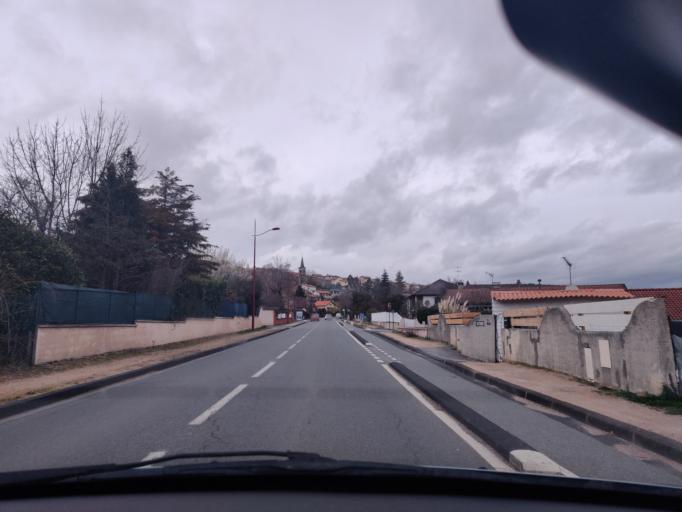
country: FR
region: Auvergne
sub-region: Departement du Puy-de-Dome
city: Enval
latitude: 45.9066
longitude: 3.0574
